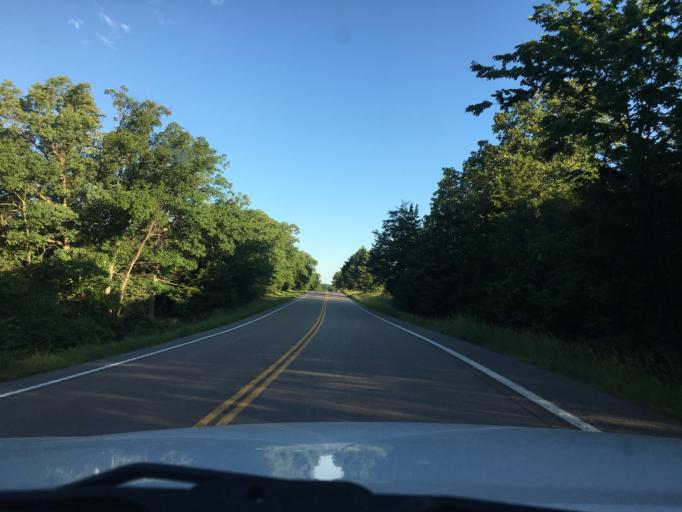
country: US
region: Missouri
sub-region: Gasconade County
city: Owensville
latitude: 38.4510
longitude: -91.4488
